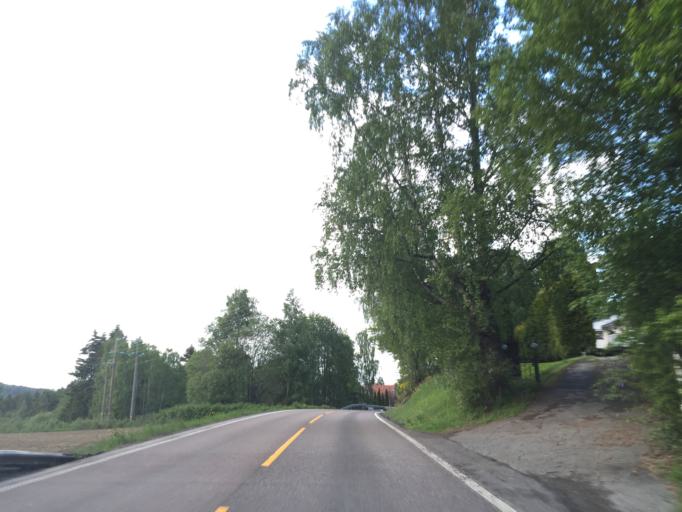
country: NO
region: Akershus
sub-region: Sorum
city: Sorumsand
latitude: 59.9661
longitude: 11.2160
